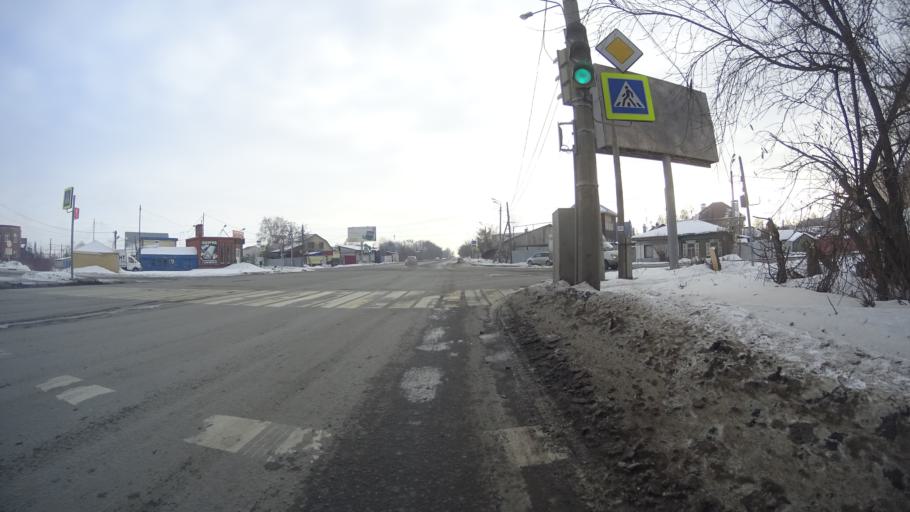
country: RU
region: Chelyabinsk
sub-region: Gorod Chelyabinsk
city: Chelyabinsk
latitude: 55.1322
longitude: 61.3853
